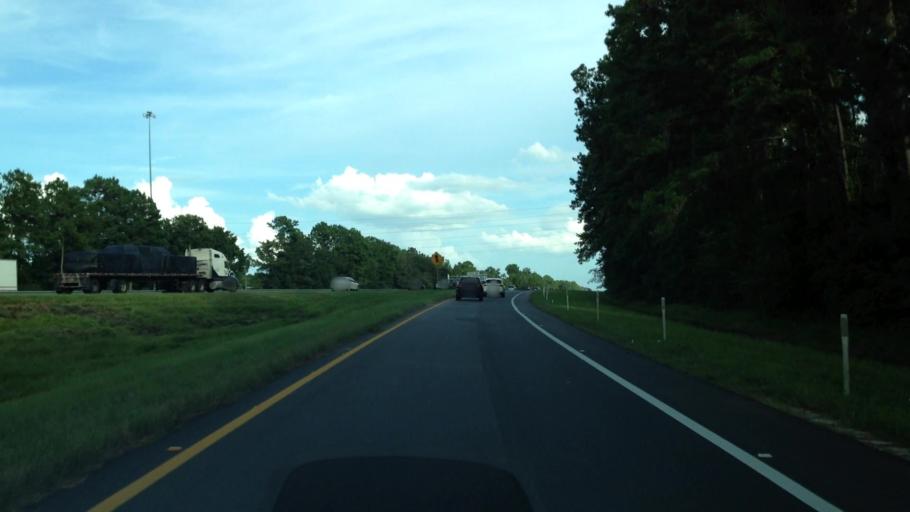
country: US
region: Florida
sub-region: Alachua County
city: Gainesville
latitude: 29.6152
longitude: -82.3852
